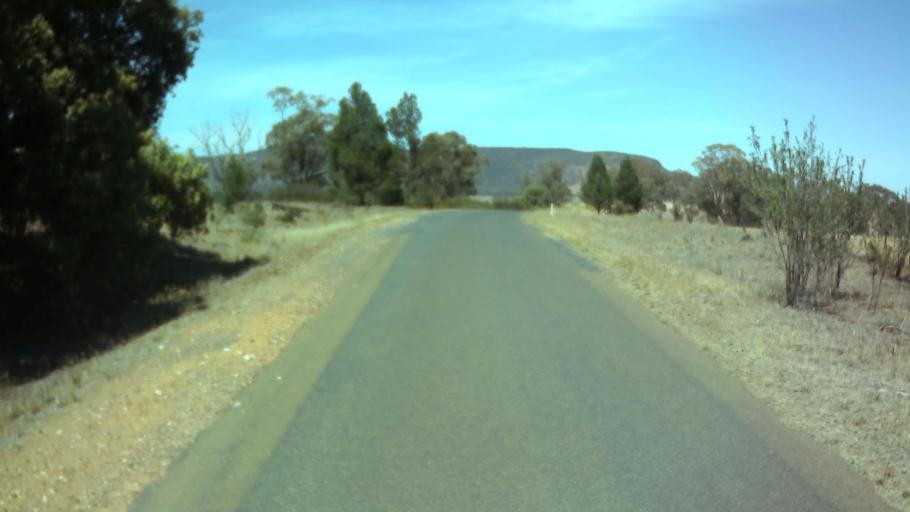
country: AU
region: New South Wales
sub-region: Weddin
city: Grenfell
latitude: -33.8648
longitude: 148.0097
